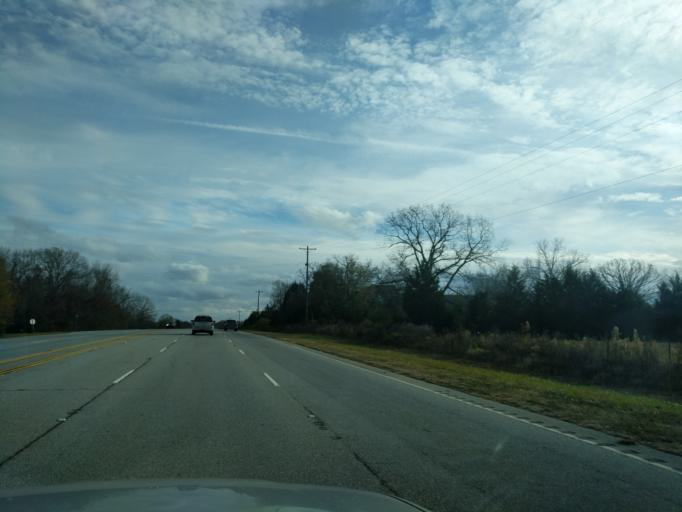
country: US
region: South Carolina
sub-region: Anderson County
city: Honea Path
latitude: 34.5228
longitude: -82.3136
